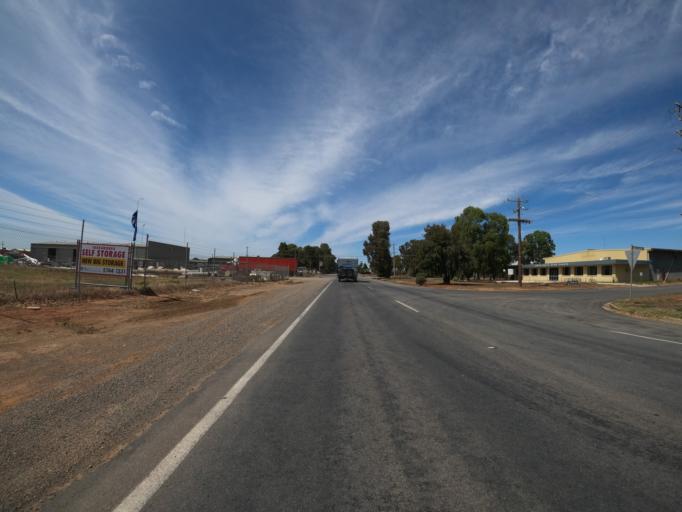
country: AU
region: Victoria
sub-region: Moira
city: Yarrawonga
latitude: -36.0296
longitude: 145.9955
